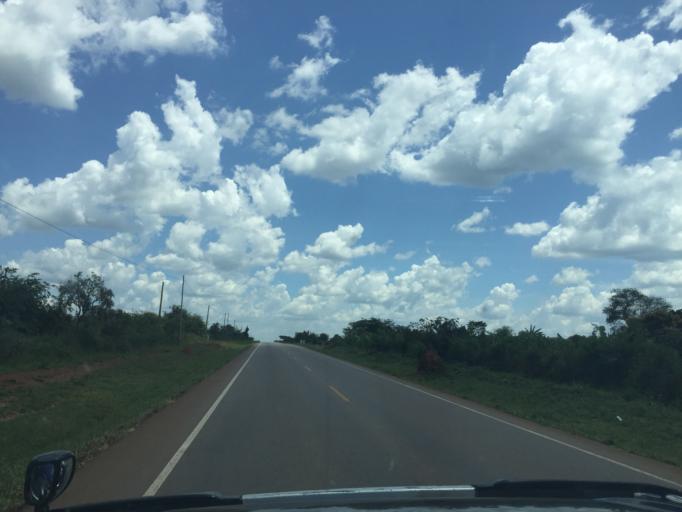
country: UG
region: Central Region
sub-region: Nakasongola District
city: Nakasongola
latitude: 1.3702
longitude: 32.3540
